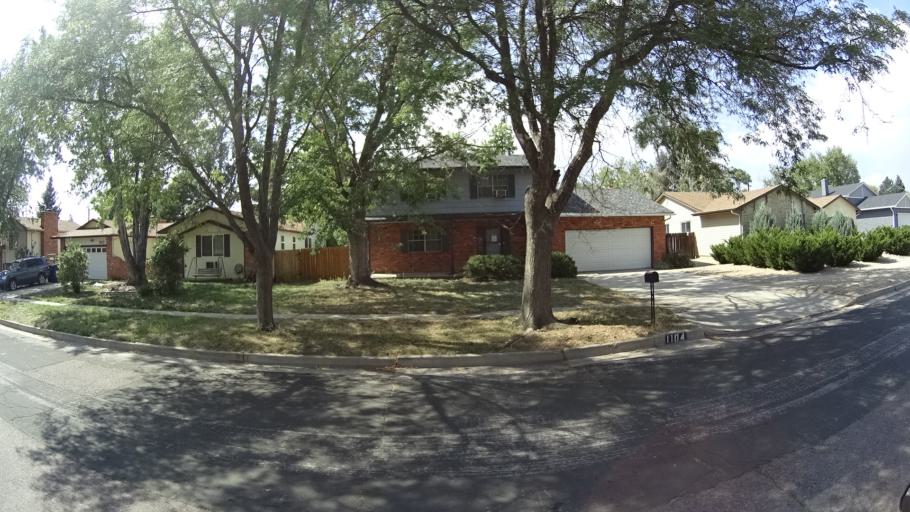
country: US
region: Colorado
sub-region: El Paso County
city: Colorado Springs
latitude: 38.8478
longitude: -104.7635
